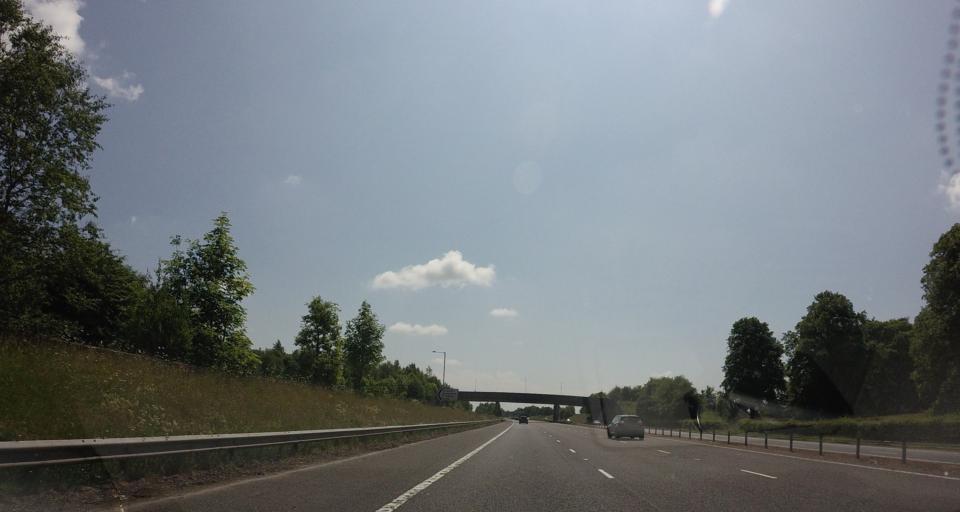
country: GB
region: Scotland
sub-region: Dumfries and Galloway
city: Lockerbie
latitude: 55.1203
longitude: -3.3624
